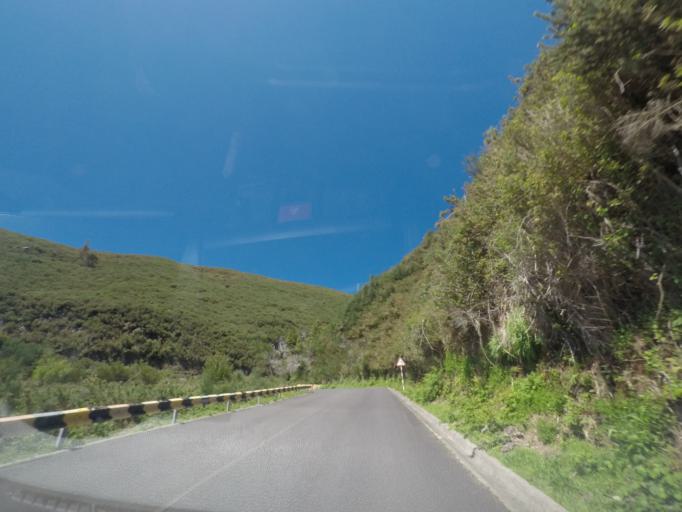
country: PT
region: Madeira
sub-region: Calheta
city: Arco da Calheta
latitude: 32.7431
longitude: -17.1274
